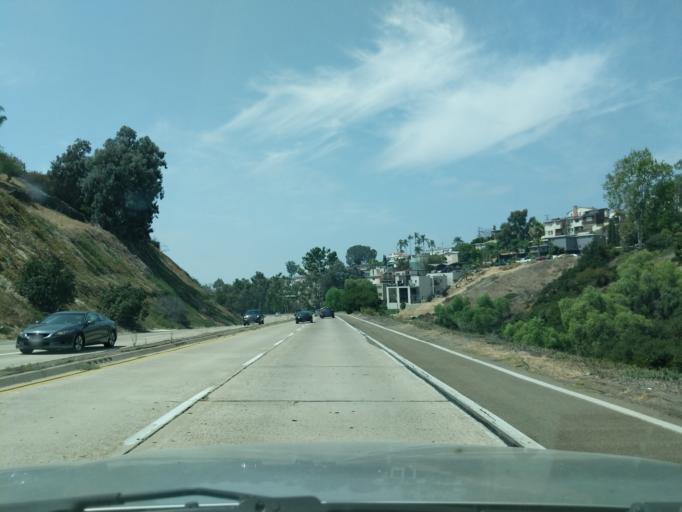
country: US
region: California
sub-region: San Diego County
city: San Diego
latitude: 32.7471
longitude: -117.1770
